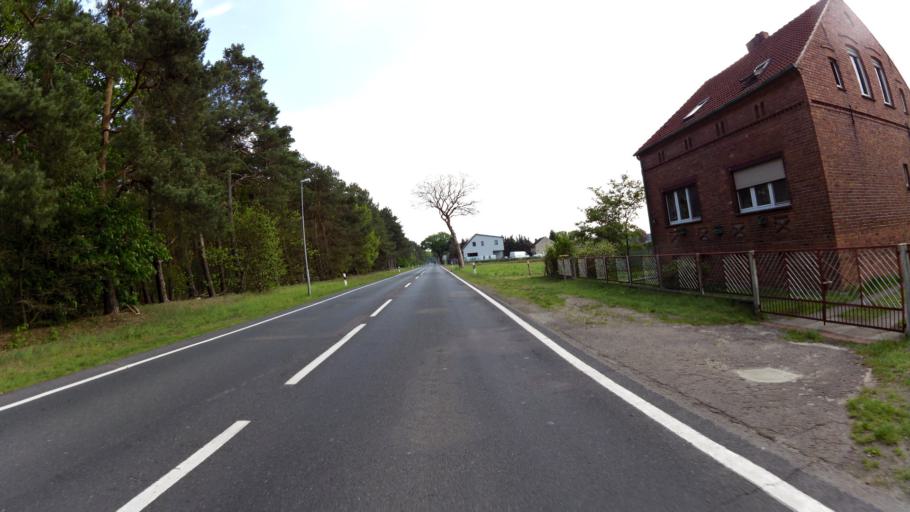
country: DE
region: Brandenburg
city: Spreenhagen
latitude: 52.3316
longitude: 13.8974
